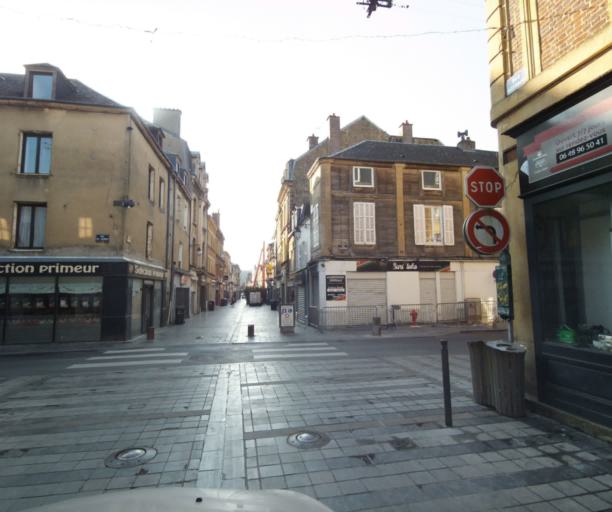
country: FR
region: Champagne-Ardenne
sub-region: Departement des Ardennes
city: Charleville-Mezieres
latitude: 49.7723
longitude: 4.7177
